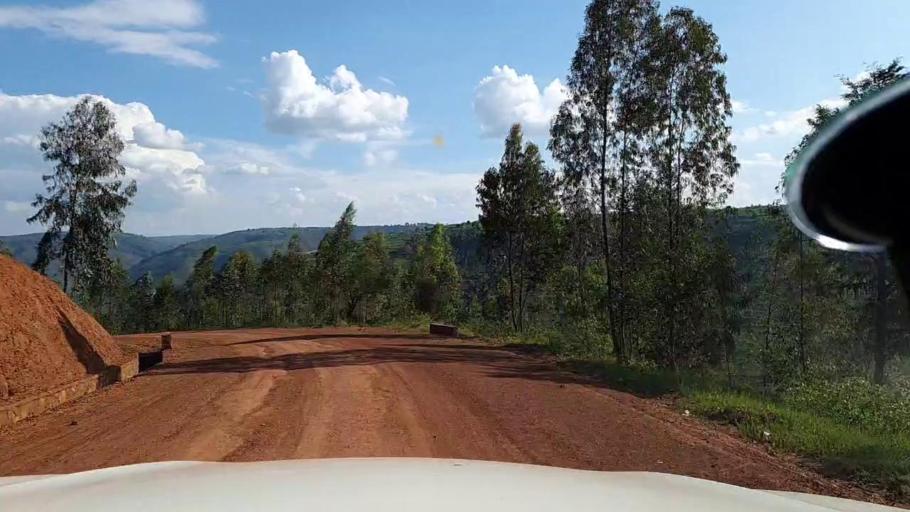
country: RW
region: Kigali
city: Kigali
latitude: -1.8427
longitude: 29.8579
